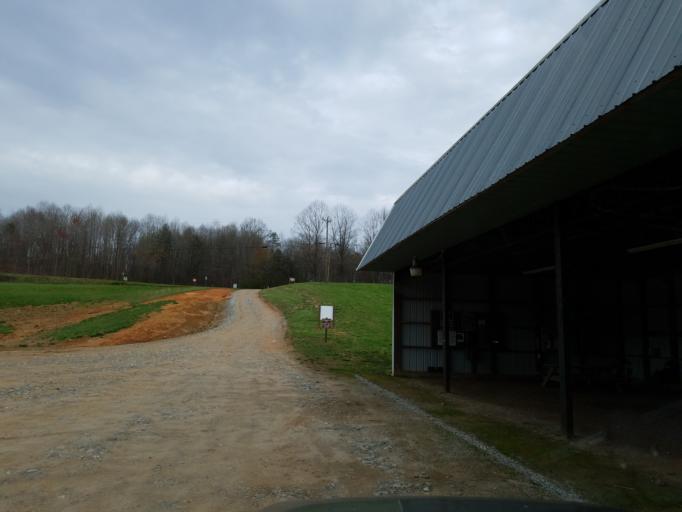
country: US
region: Georgia
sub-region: Dawson County
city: Dawsonville
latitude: 34.5257
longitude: -84.2542
